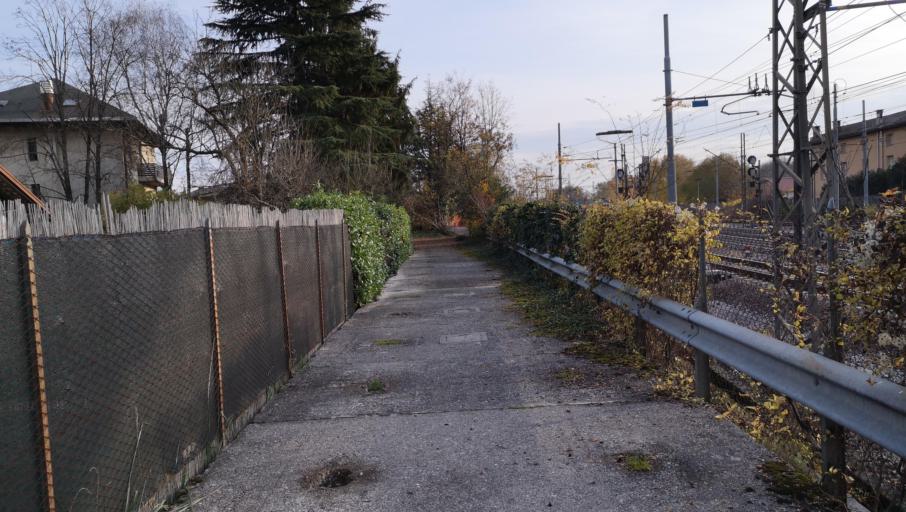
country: IT
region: Friuli Venezia Giulia
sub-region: Provincia di Udine
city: Magnano in Riviera
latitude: 46.2126
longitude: 13.1945
